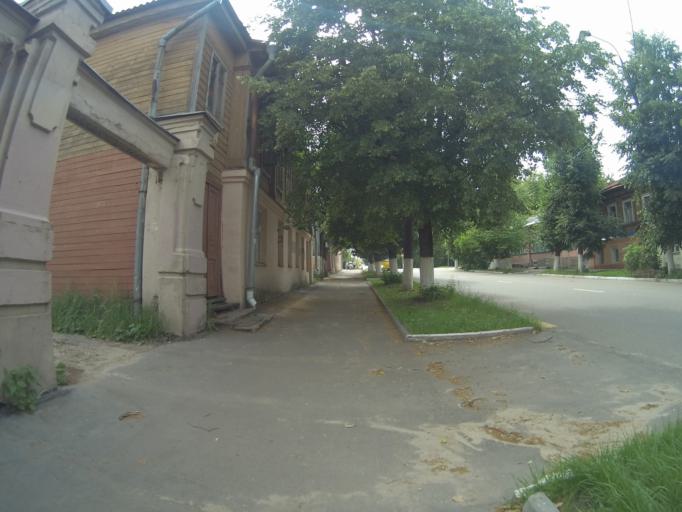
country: RU
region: Vladimir
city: Vladimir
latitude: 56.1292
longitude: 40.3987
